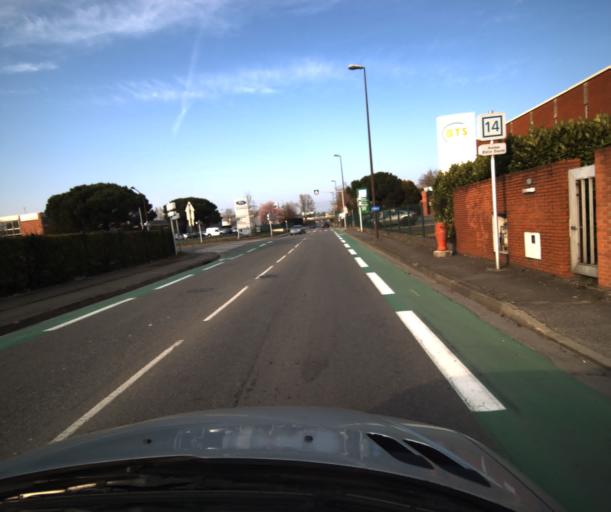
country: FR
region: Midi-Pyrenees
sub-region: Departement de la Haute-Garonne
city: Ramonville-Saint-Agne
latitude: 43.5663
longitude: 1.4894
